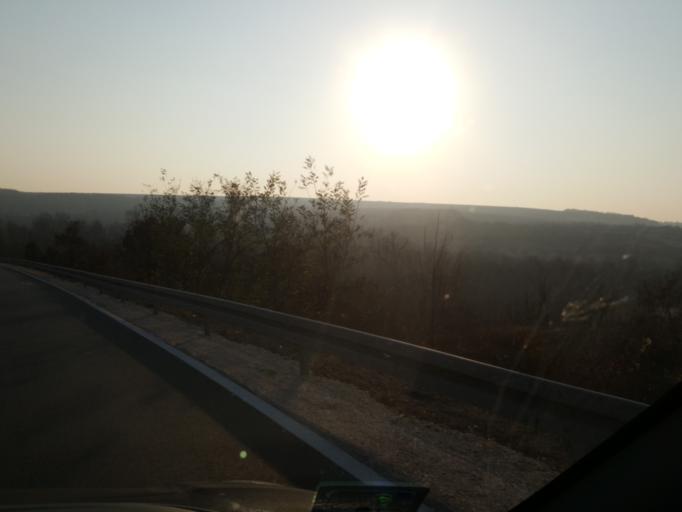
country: RS
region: Central Serbia
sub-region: Zajecarski Okrug
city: Zajecar
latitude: 43.9858
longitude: 22.2958
